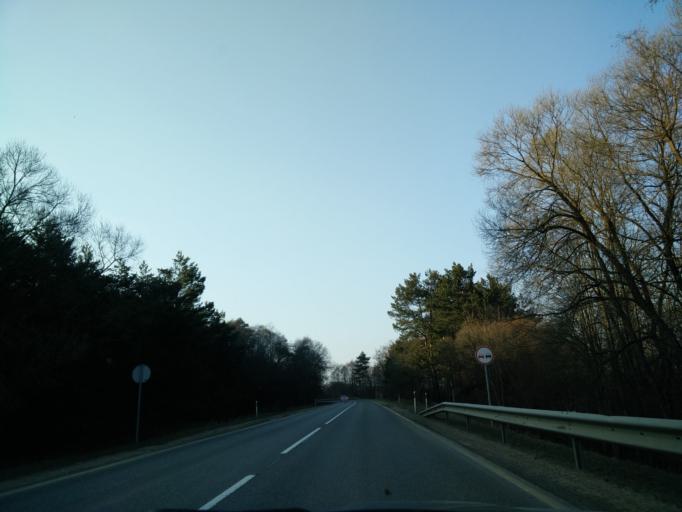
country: LT
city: Trakai
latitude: 54.6597
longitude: 24.9154
